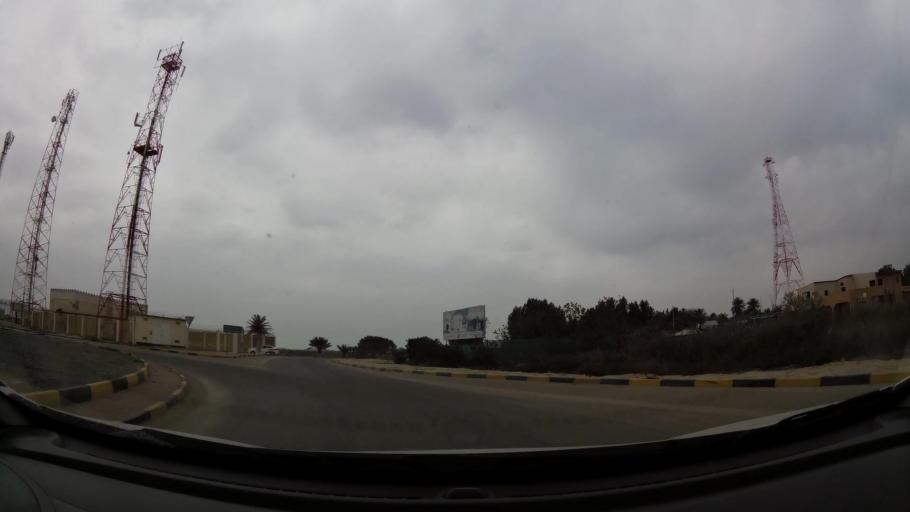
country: BH
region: Central Governorate
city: Dar Kulayb
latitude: 25.9960
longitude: 50.4683
